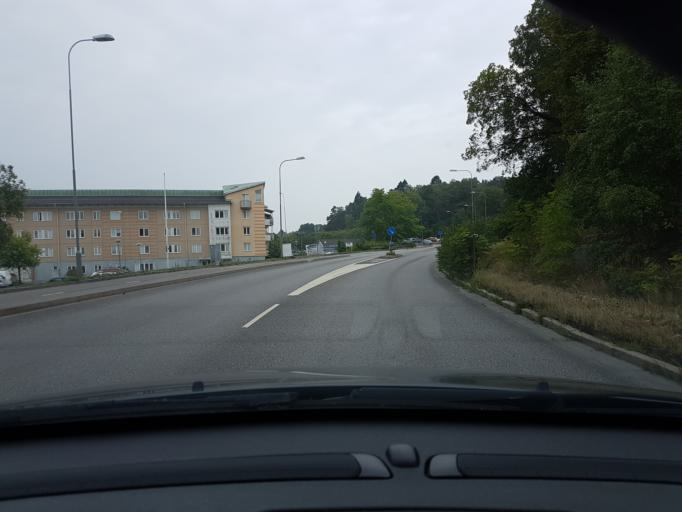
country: SE
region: Vaestra Goetaland
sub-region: Goteborg
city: Majorna
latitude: 57.6449
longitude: 11.8948
